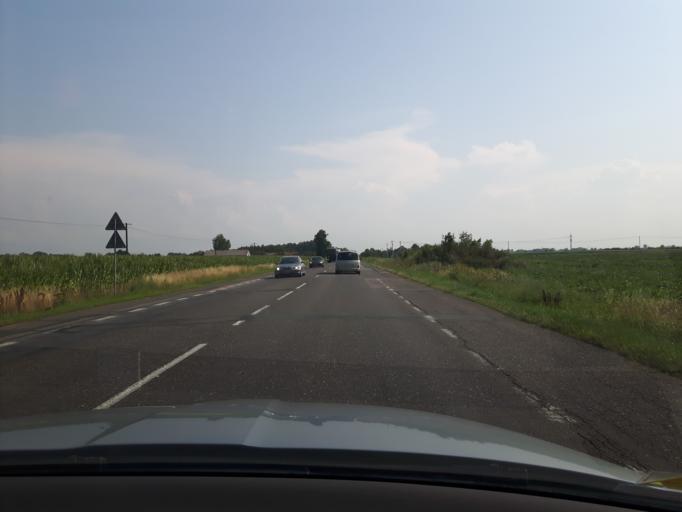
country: PL
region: Masovian Voivodeship
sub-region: Powiat plonski
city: Plonsk
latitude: 52.6713
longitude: 20.3722
